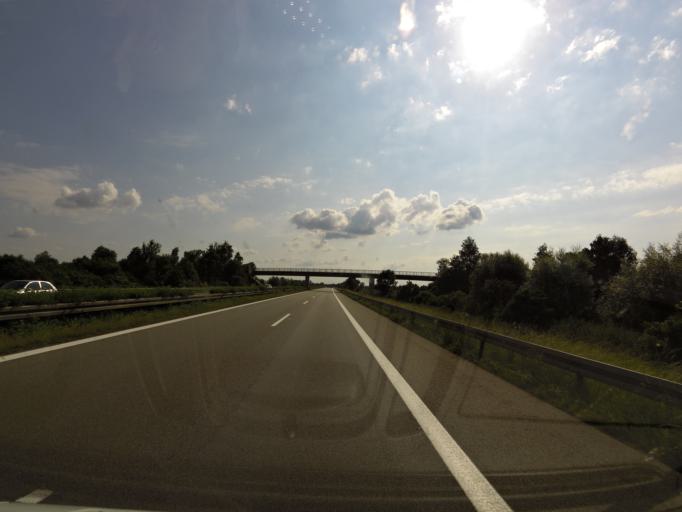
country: DE
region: Bavaria
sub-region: Lower Bavaria
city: Wallersdorf
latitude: 48.7177
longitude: 12.7142
